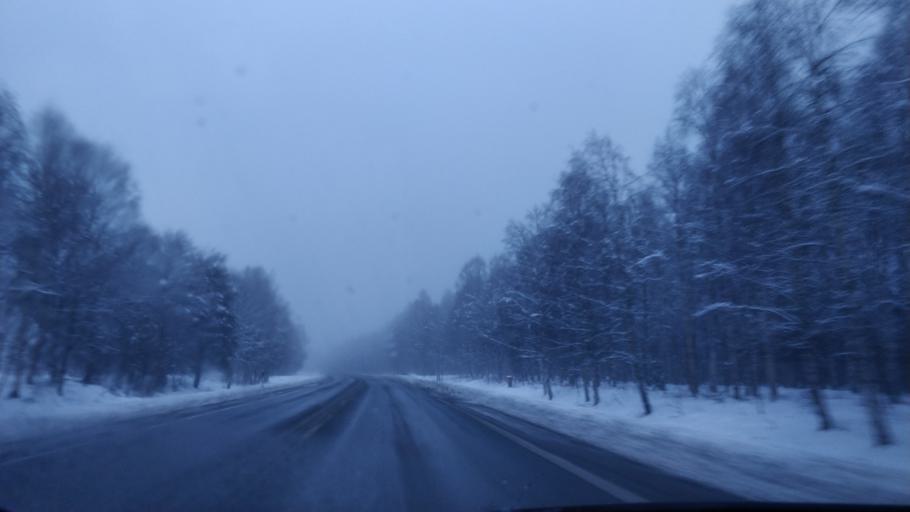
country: FI
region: Lapland
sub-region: Kemi-Tornio
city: Tervola
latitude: 66.1527
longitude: 25.0299
